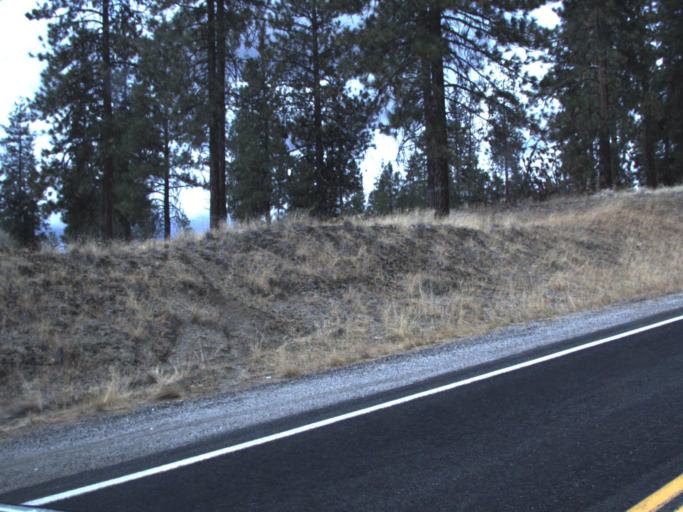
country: US
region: Washington
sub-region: Spokane County
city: Fairchild Air Force Base
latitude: 47.8797
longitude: -117.8393
